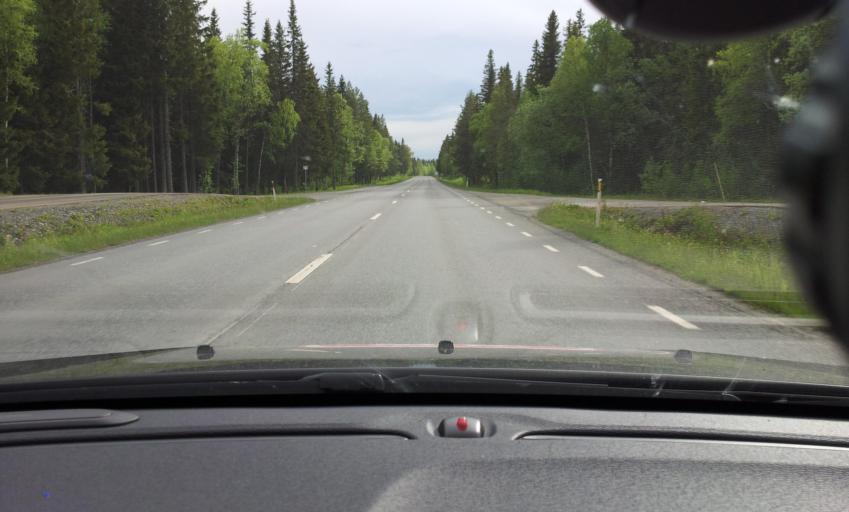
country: SE
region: Jaemtland
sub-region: OEstersunds Kommun
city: Ostersund
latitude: 63.1876
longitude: 14.7390
